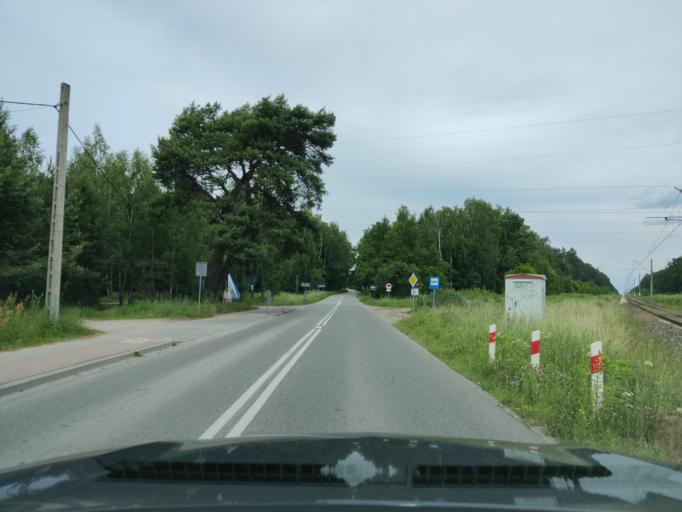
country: PL
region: Masovian Voivodeship
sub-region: Powiat wyszkowski
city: Wyszkow
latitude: 52.6210
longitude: 21.4523
